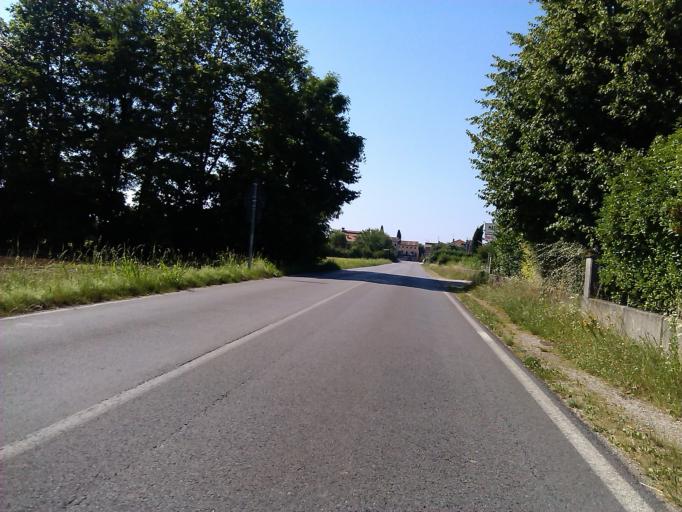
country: IT
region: Veneto
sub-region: Provincia di Vicenza
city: Cassola
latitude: 45.7393
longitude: 11.8135
